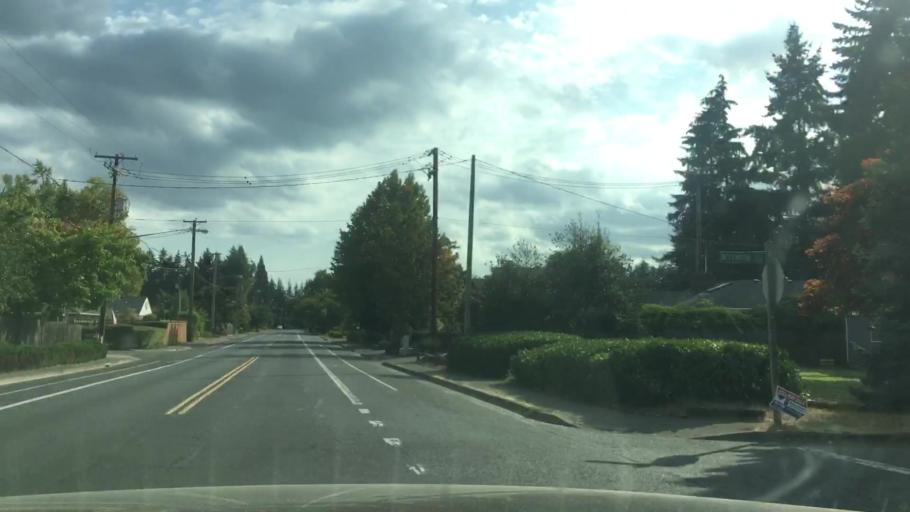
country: US
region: Oregon
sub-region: Lane County
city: Eugene
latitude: 44.0873
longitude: -123.0881
